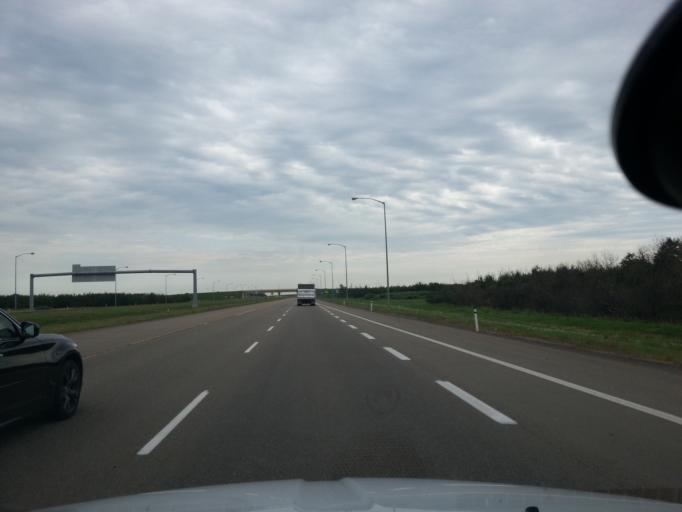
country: CA
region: Alberta
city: Edmonton
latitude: 53.6467
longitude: -113.4776
